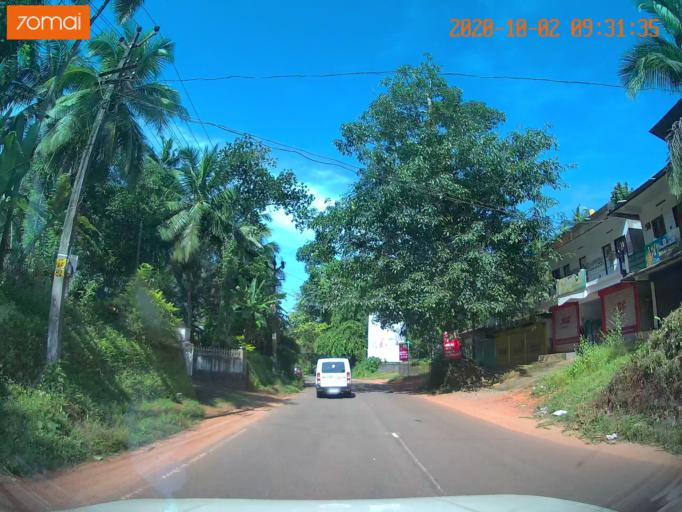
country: IN
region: Kerala
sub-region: Kozhikode
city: Nadapuram
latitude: 11.6243
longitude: 75.7597
